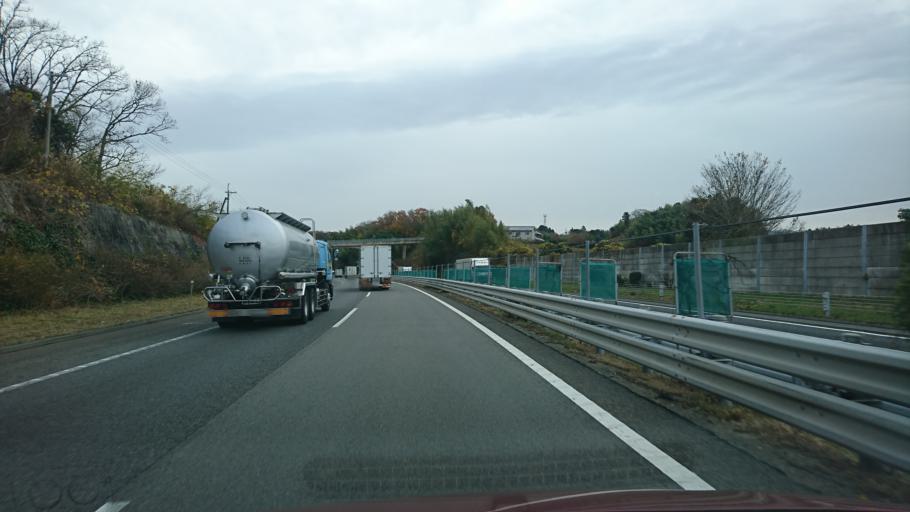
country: JP
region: Hyogo
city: Sandacho
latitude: 34.8270
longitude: 135.1749
